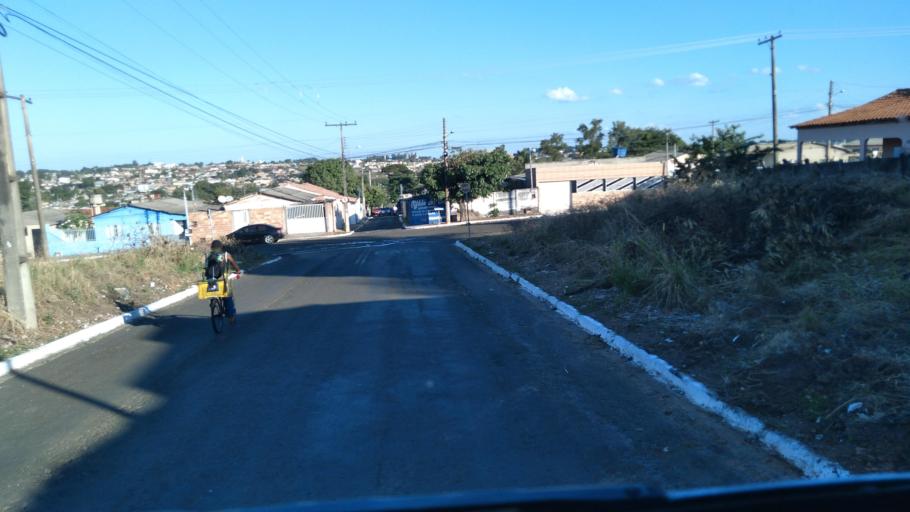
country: BR
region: Goias
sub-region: Mineiros
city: Mineiros
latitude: -17.5598
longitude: -52.5469
